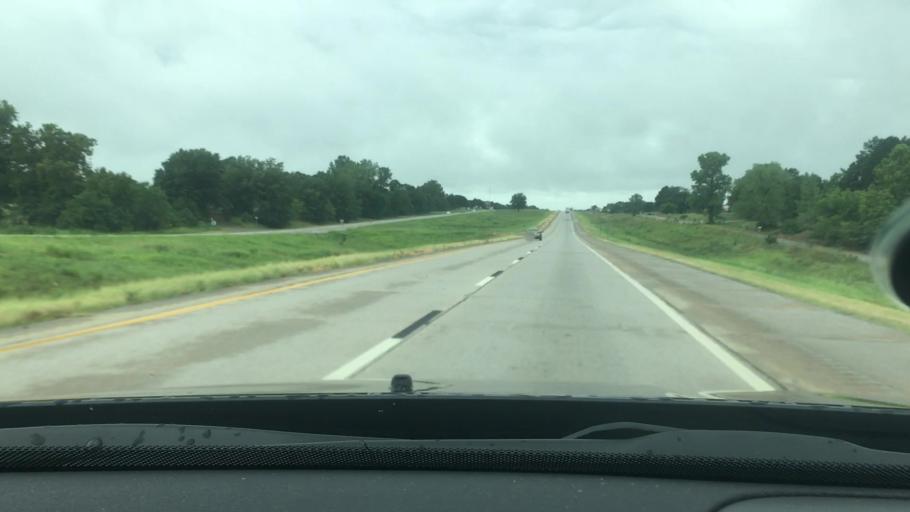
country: US
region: Oklahoma
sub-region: Atoka County
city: Atoka
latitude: 34.2125
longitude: -96.2329
